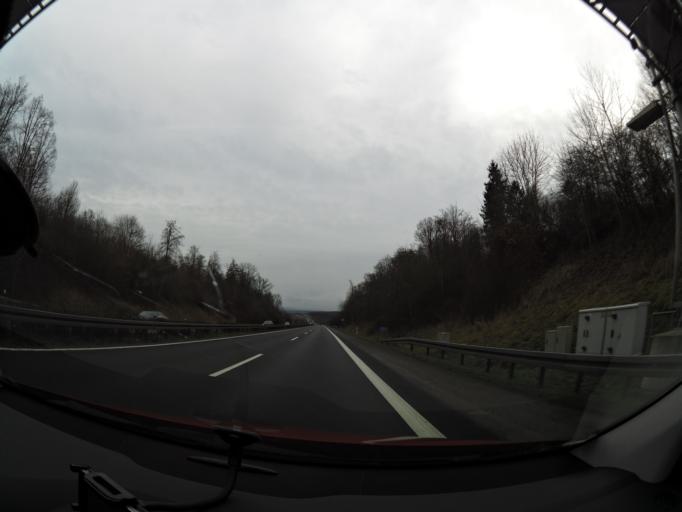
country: DE
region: Lower Saxony
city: Gielde
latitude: 52.0551
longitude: 10.5058
